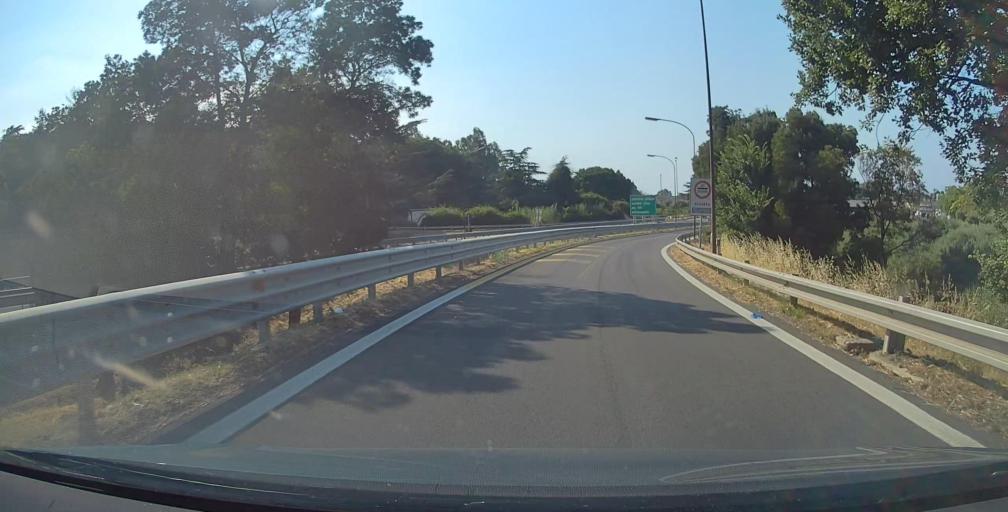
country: IT
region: Sicily
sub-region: Messina
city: Patti
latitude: 38.1441
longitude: 15.0000
